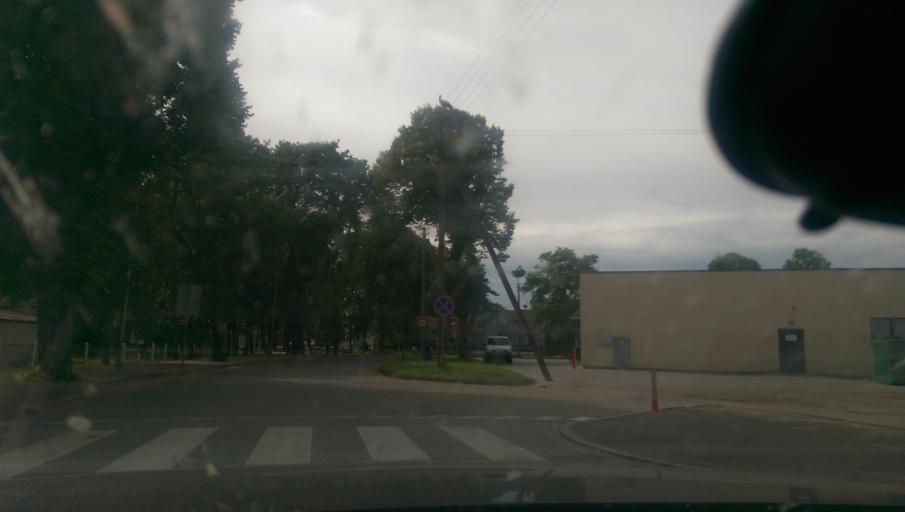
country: LT
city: Rusne
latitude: 55.2984
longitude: 21.3741
